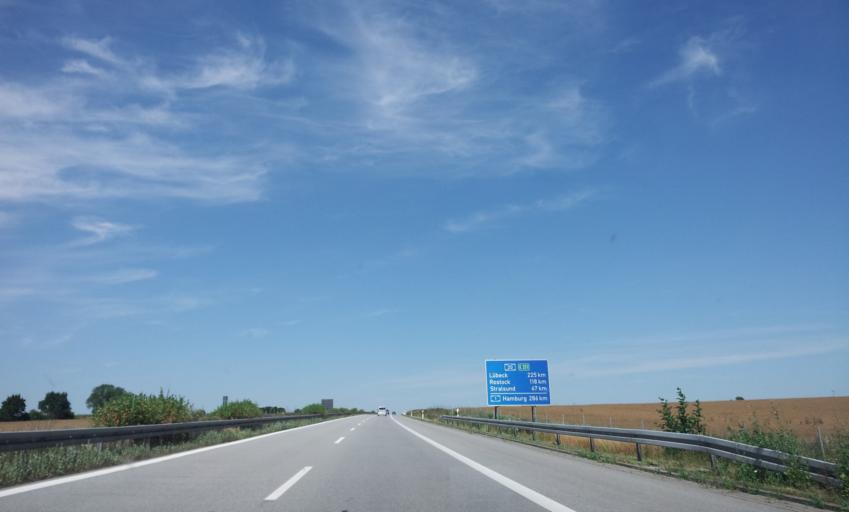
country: DE
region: Mecklenburg-Vorpommern
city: Burow
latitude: 53.7985
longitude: 13.3220
